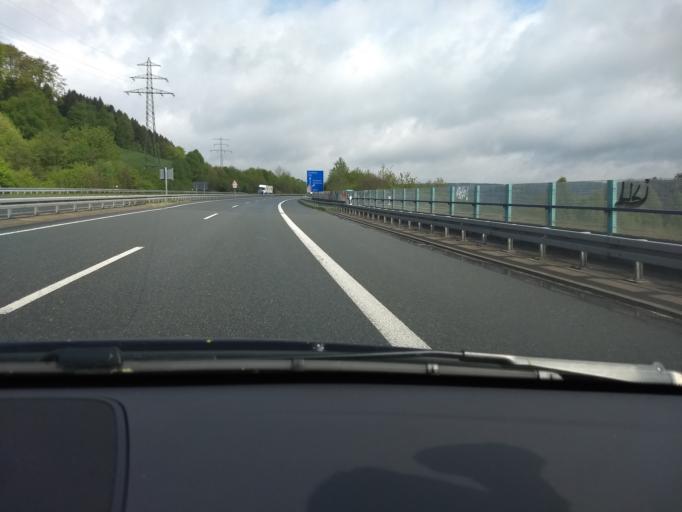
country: DE
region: North Rhine-Westphalia
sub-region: Regierungsbezirk Arnsberg
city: Arnsberg
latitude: 51.3728
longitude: 8.1564
